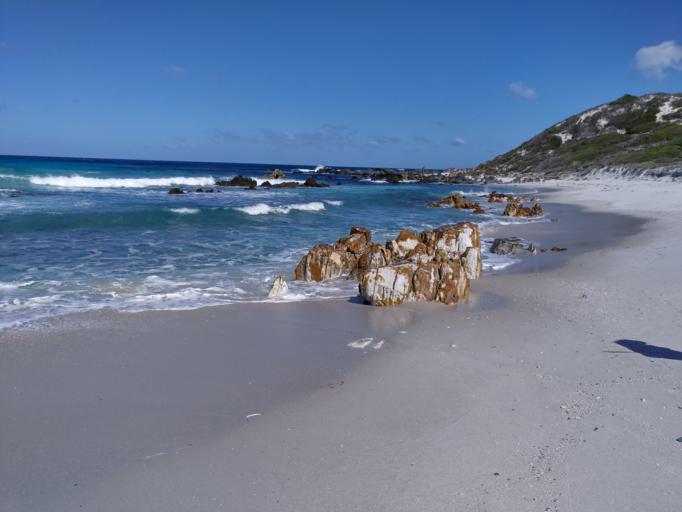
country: AU
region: Western Australia
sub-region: Ravensthorpe
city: Ravensthorpe
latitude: -33.9681
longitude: 119.9059
